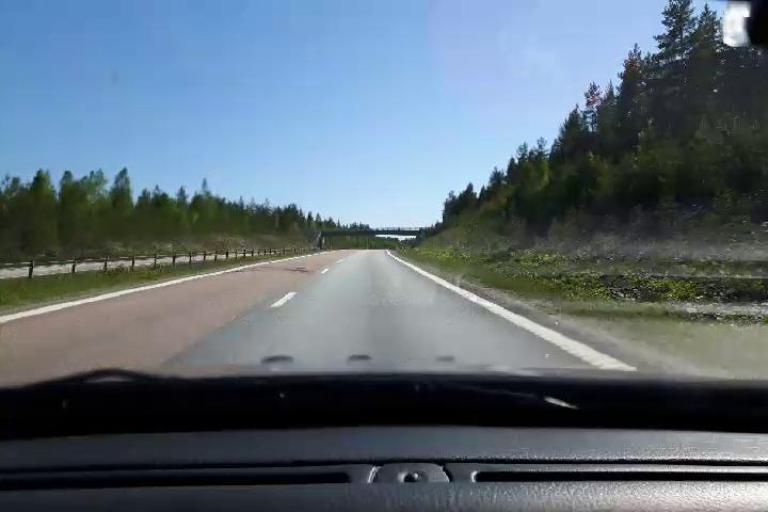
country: SE
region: Gaevleborg
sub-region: Soderhamns Kommun
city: Soderhamn
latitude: 61.4703
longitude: 16.9900
